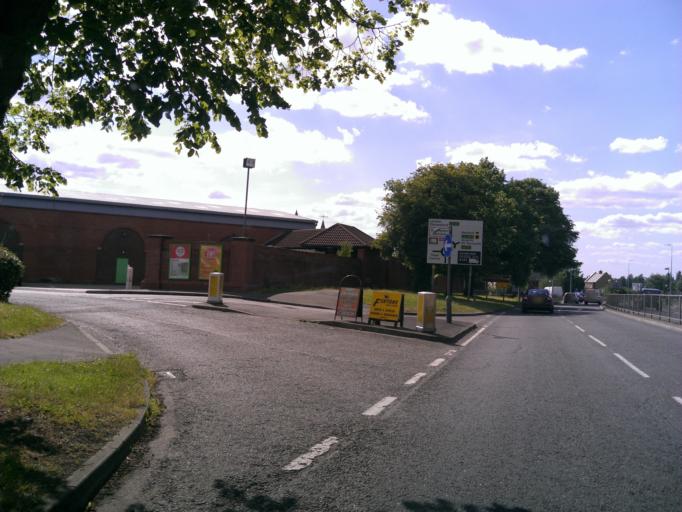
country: GB
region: England
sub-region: Essex
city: Colchester
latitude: 51.8922
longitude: 0.9201
